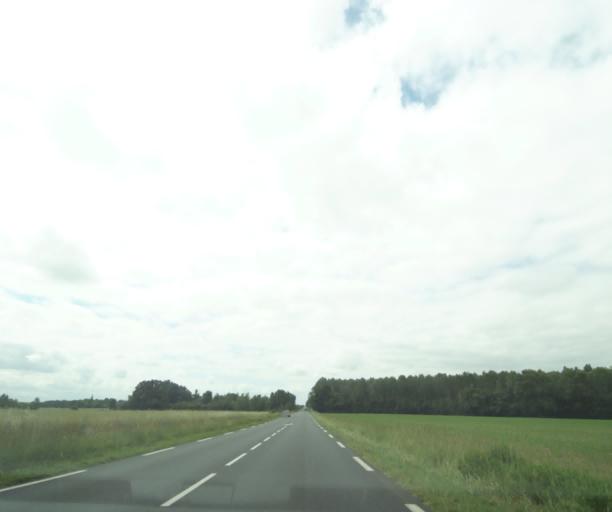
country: FR
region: Pays de la Loire
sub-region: Departement de Maine-et-Loire
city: Montreuil-Bellay
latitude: 47.1106
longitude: -0.1641
